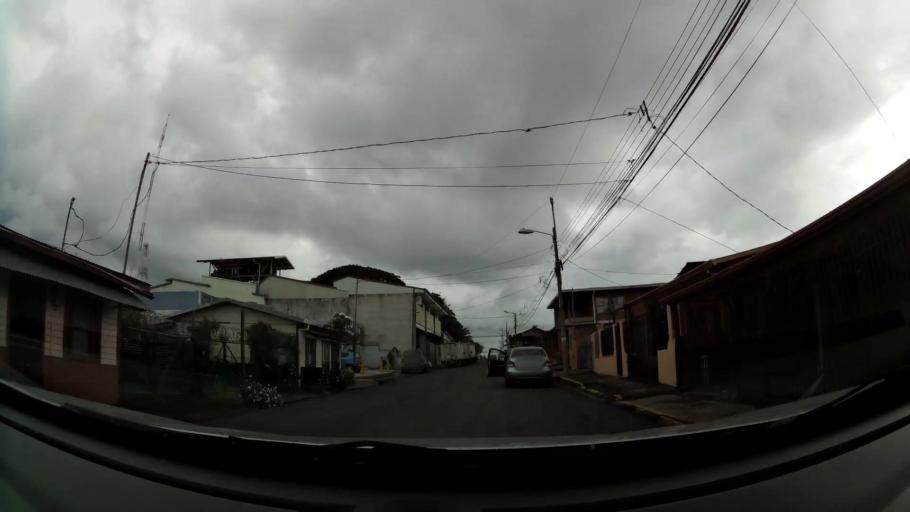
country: CR
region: Puntarenas
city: Esparza
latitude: 9.9902
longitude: -84.6680
